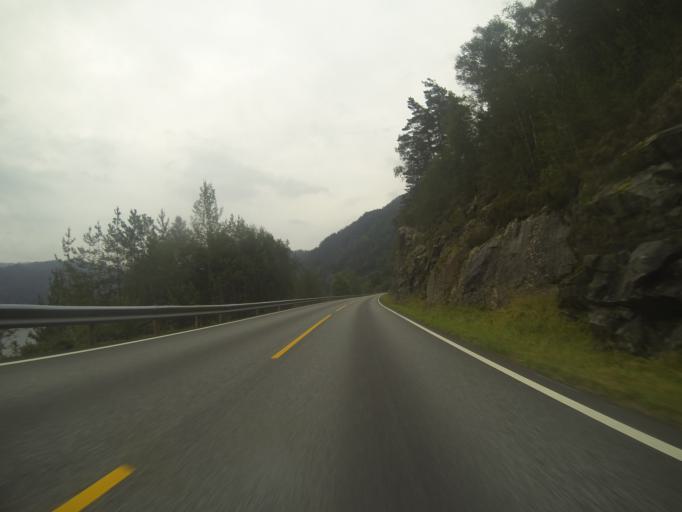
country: NO
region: Rogaland
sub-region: Suldal
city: Sand
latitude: 59.4726
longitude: 6.1887
